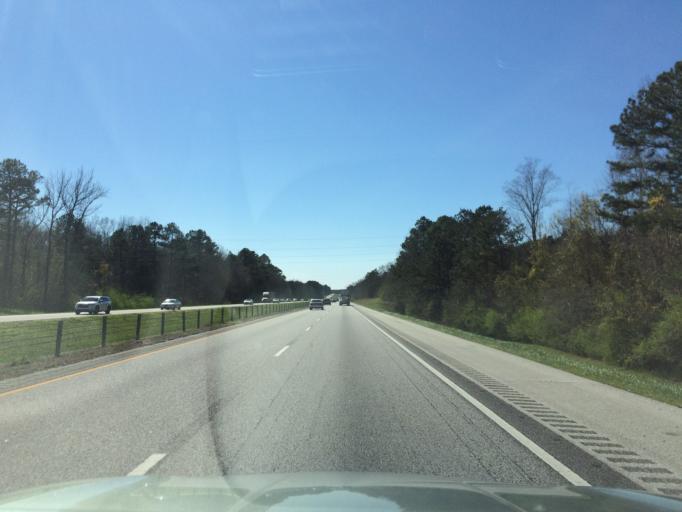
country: US
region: Alabama
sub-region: Lee County
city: Auburn
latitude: 32.5378
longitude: -85.5449
